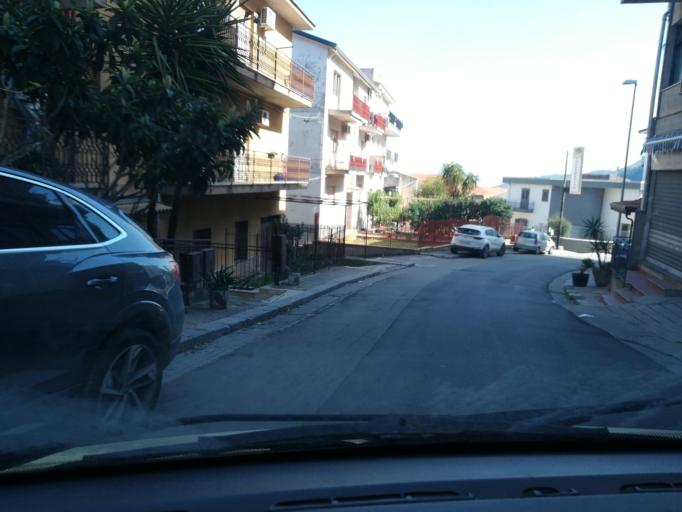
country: IT
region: Sicily
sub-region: Palermo
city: Altofonte
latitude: 38.0442
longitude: 13.2939
